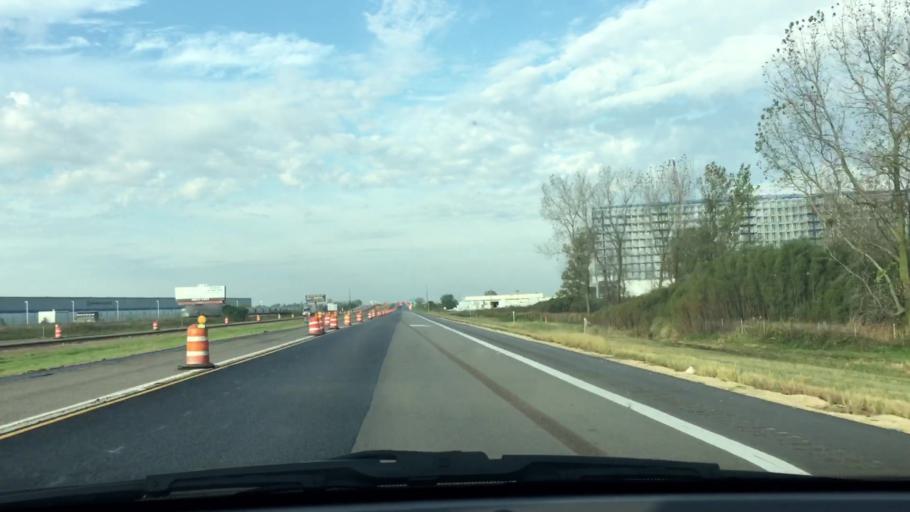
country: US
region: Illinois
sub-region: Ogle County
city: Rochelle
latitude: 41.9041
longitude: -89.0307
